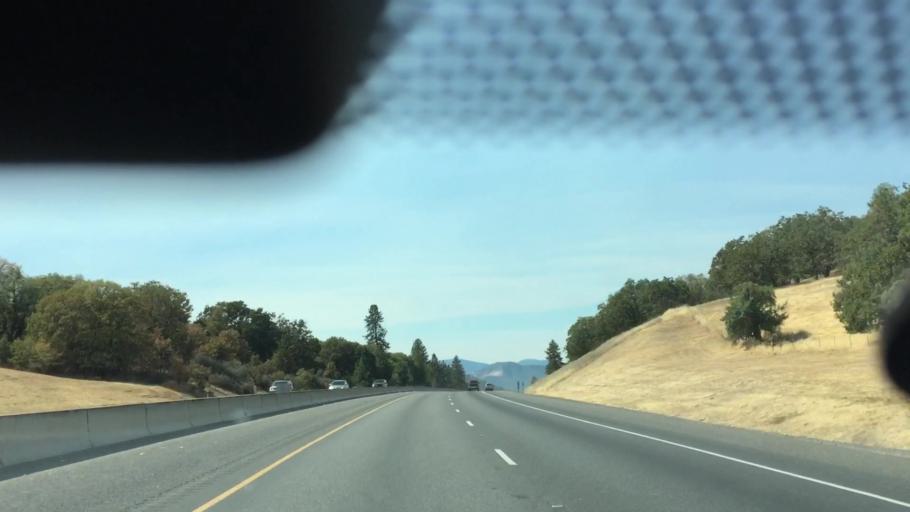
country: US
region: Oregon
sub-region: Jackson County
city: Gold Hill
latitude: 42.4126
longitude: -122.9887
